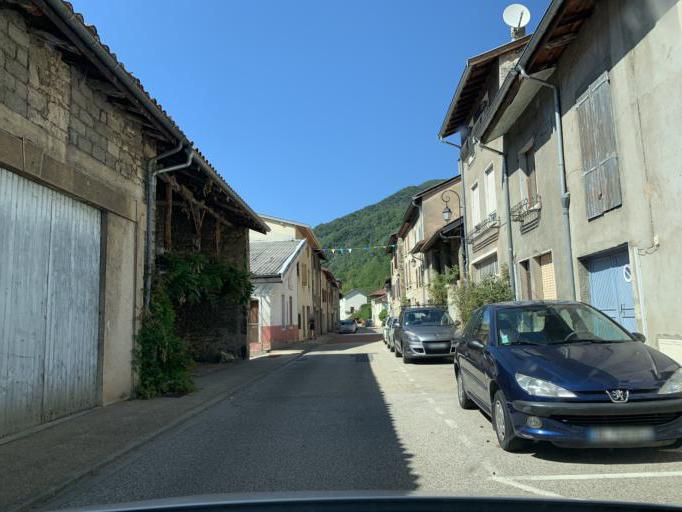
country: FR
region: Rhone-Alpes
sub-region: Departement de l'Ain
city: Vaux-en-Bugey
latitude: 45.9233
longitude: 5.3957
